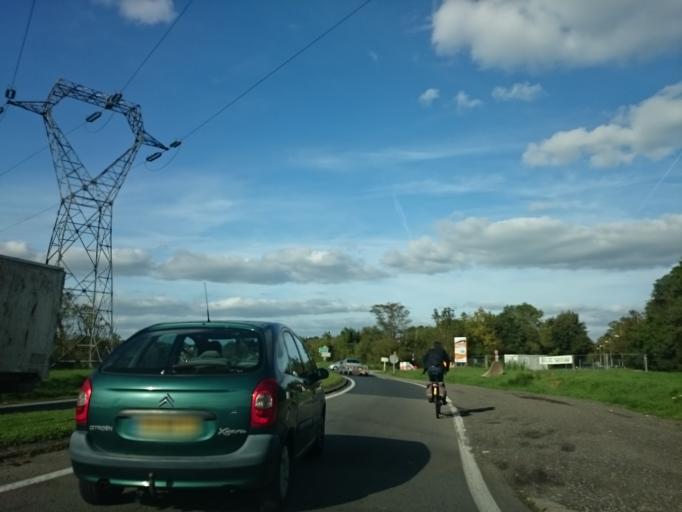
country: FR
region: Pays de la Loire
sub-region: Departement de la Loire-Atlantique
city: Indre
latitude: 47.2014
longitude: -1.6674
